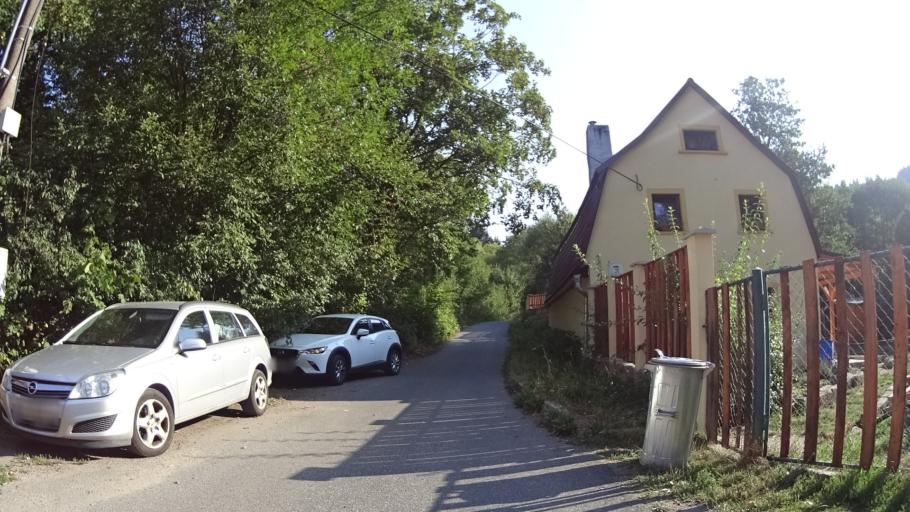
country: CZ
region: Liberecky
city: Hodkovice nad Mohelkou
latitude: 50.6760
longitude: 15.0979
